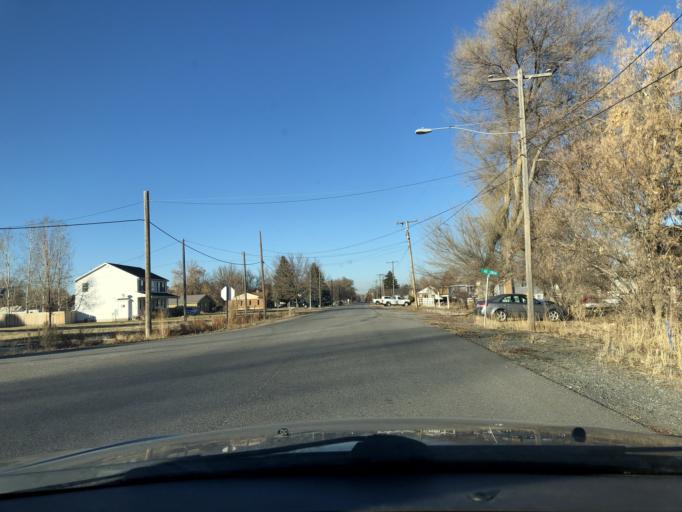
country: US
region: Utah
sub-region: Cache County
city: Wellsville
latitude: 41.6324
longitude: -111.9318
